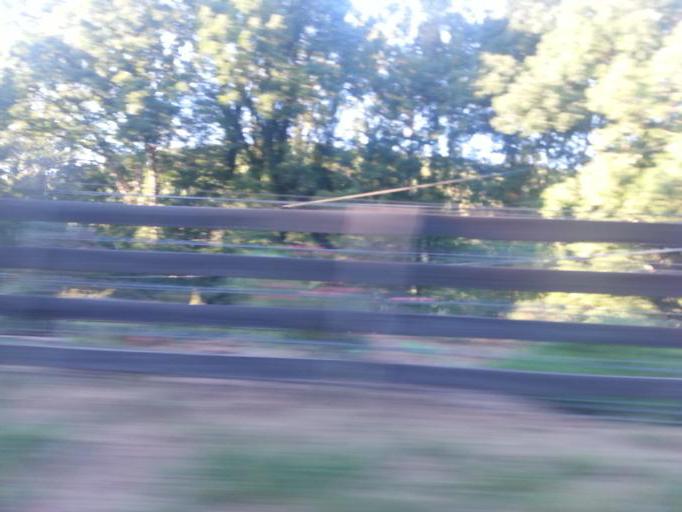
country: US
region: Tennessee
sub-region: Blount County
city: Wildwood
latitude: 35.8534
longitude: -83.8767
